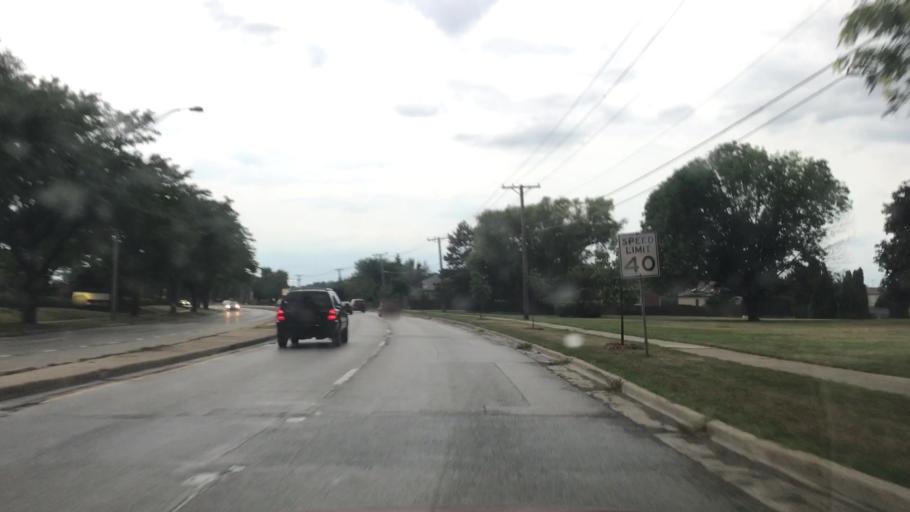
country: US
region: Illinois
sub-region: Cook County
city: Mount Prospect
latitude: 42.0508
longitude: -87.9706
